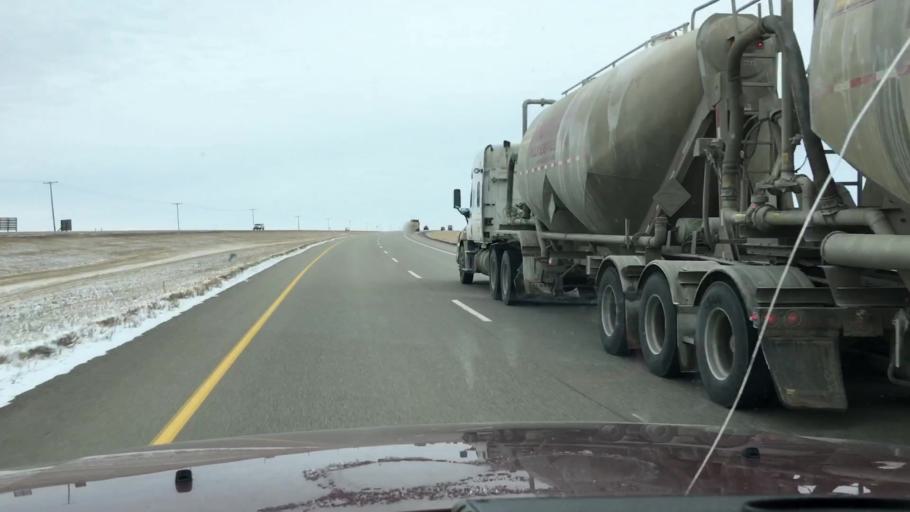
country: CA
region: Saskatchewan
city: Watrous
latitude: 51.2342
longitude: -105.9621
